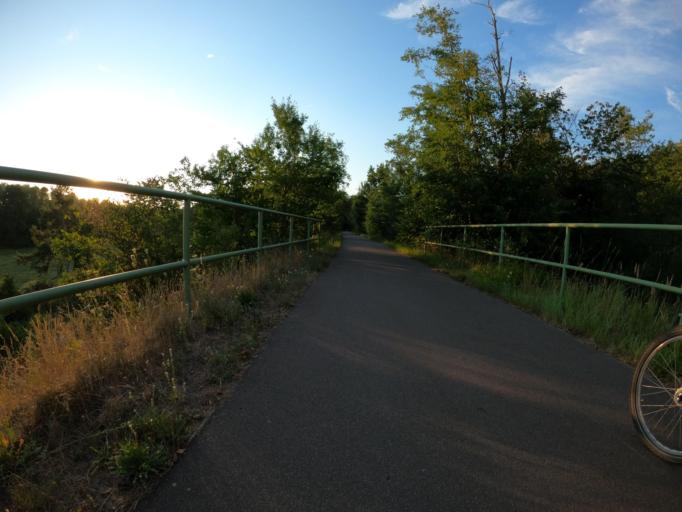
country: DE
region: Brandenburg
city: Templin
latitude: 53.1616
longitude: 13.5239
